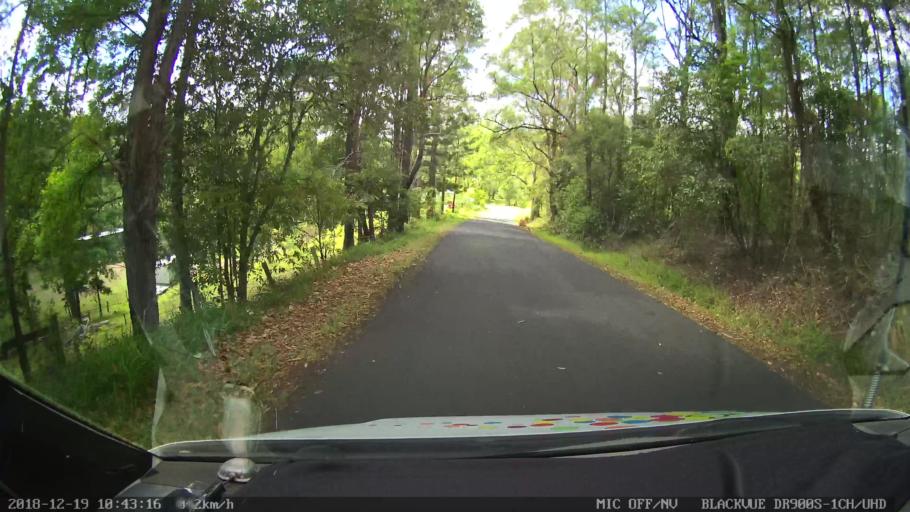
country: AU
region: New South Wales
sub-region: Lismore Municipality
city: Nimbin
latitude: -28.5941
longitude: 153.1726
